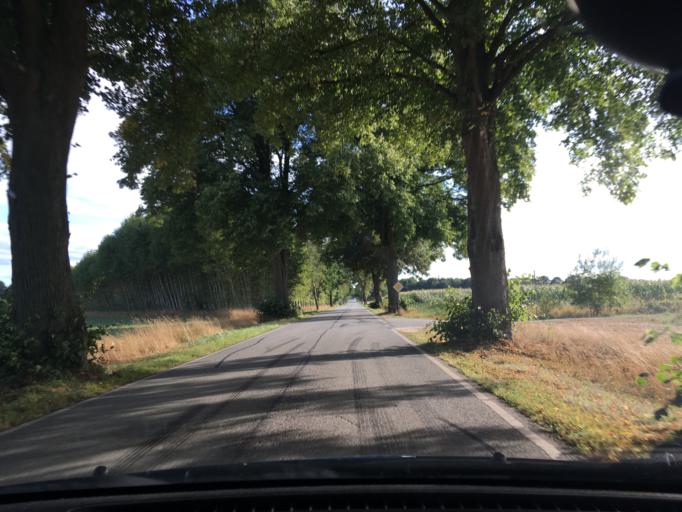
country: DE
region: Lower Saxony
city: Brackel
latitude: 53.3090
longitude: 10.0523
